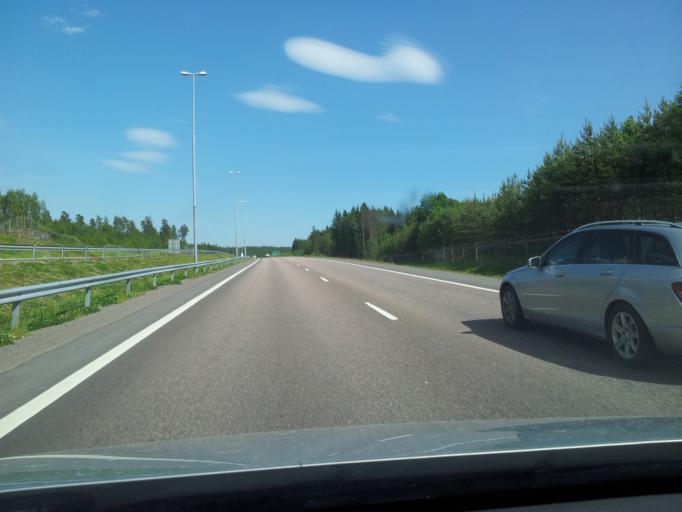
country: FI
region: Uusimaa
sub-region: Loviisa
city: Perna
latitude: 60.4912
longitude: 25.9838
